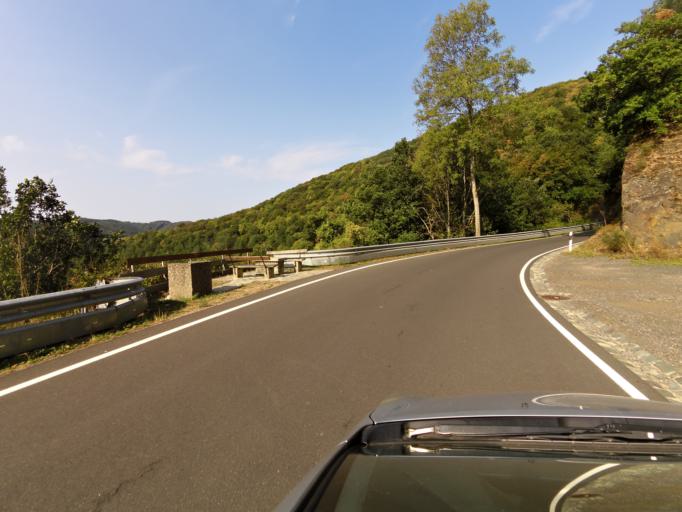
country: LU
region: Diekirch
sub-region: Canton de Wiltz
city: Goesdorf
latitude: 49.9118
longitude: 5.9796
